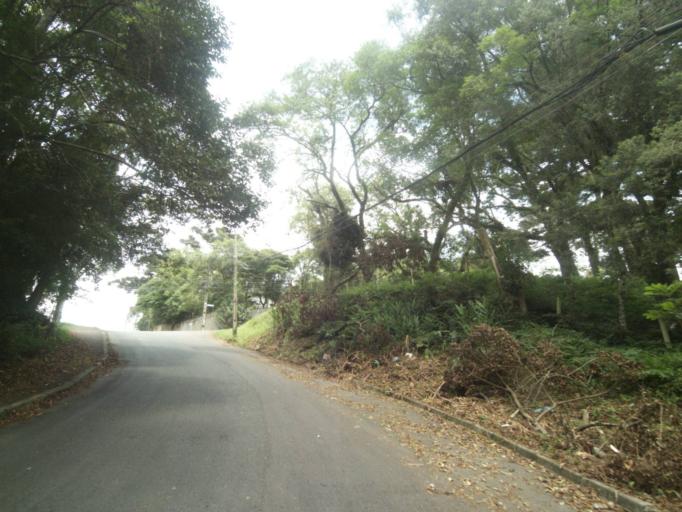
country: BR
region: Parana
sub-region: Curitiba
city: Curitiba
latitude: -25.3878
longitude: -49.2795
